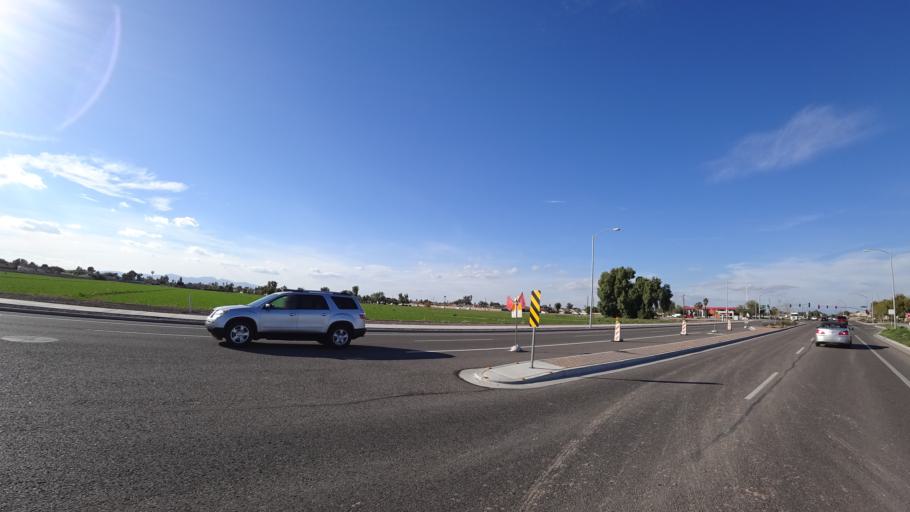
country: US
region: Arizona
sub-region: Maricopa County
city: Peoria
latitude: 33.5645
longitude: -112.2377
